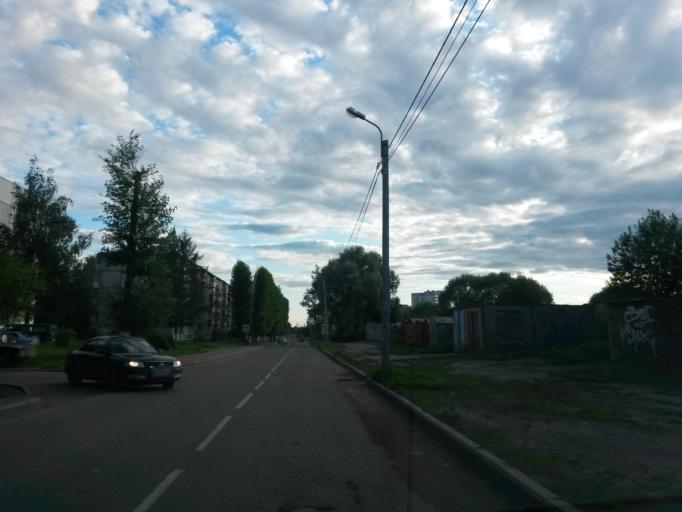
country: RU
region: Jaroslavl
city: Yaroslavl
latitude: 57.6872
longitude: 39.7745
